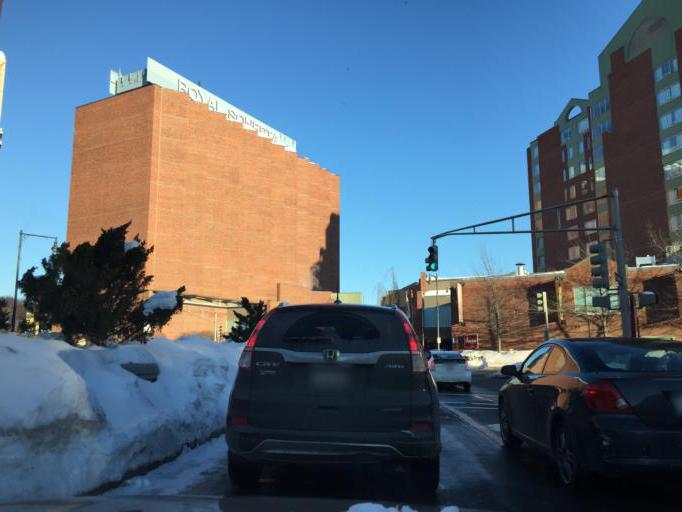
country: US
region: Massachusetts
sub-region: Suffolk County
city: Boston
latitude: 42.3670
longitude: -71.0760
